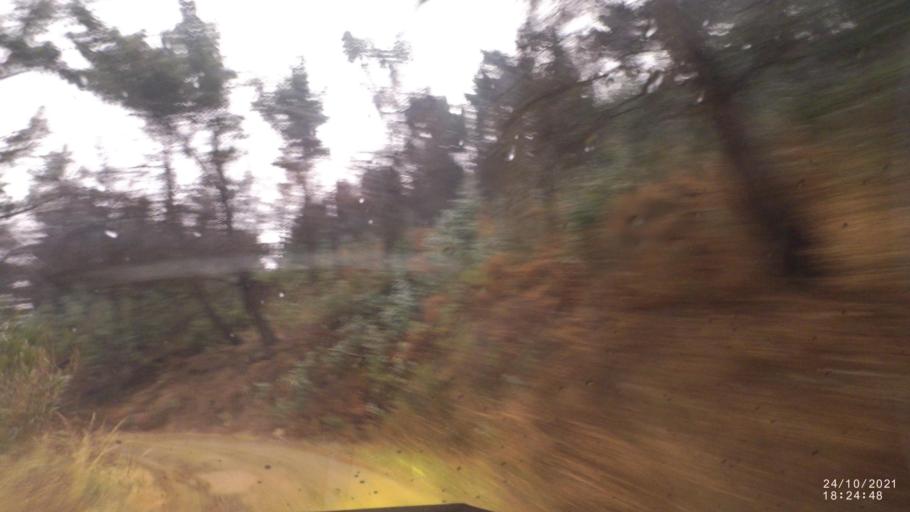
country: BO
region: Cochabamba
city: Cochabamba
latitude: -17.3379
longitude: -66.1396
